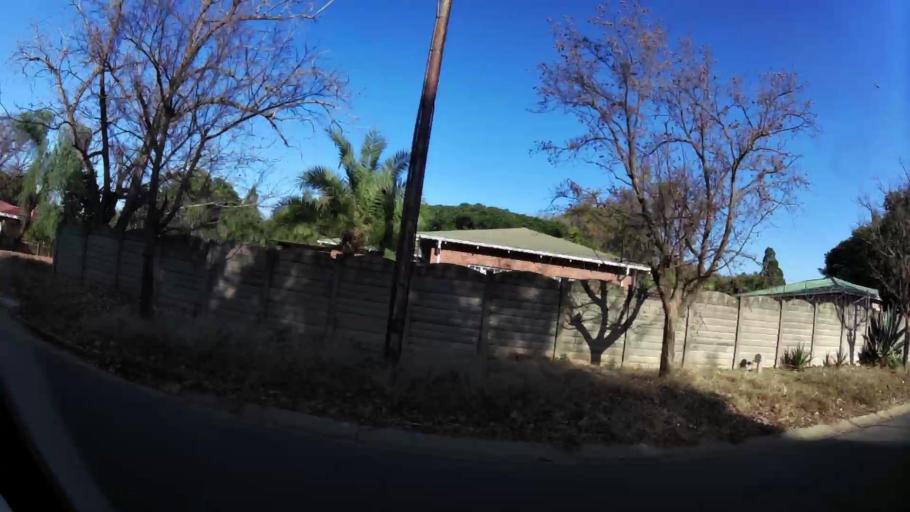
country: ZA
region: North-West
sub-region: Bojanala Platinum District Municipality
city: Rustenburg
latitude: -25.6866
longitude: 27.2300
